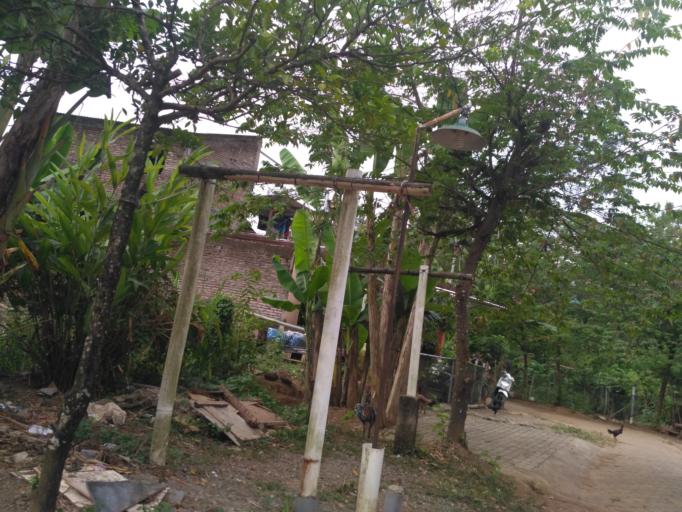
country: ID
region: Central Java
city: Ungaran
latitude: -7.0819
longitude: 110.4261
